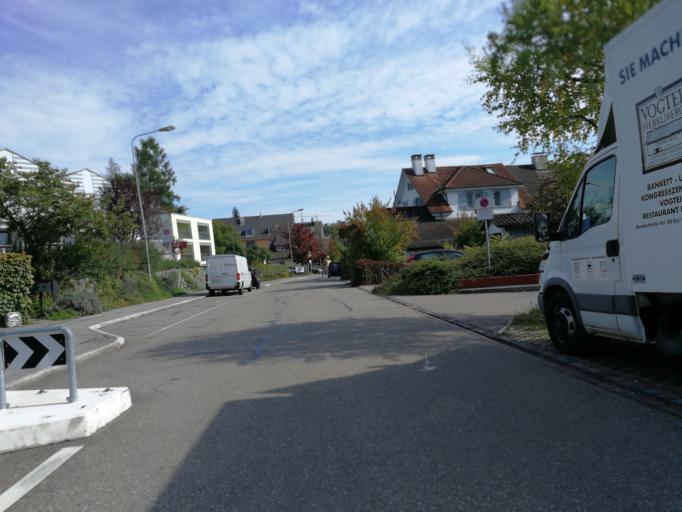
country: CH
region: Zurich
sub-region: Bezirk Meilen
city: Maennedorf / Dorfkern
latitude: 47.2575
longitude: 8.6870
